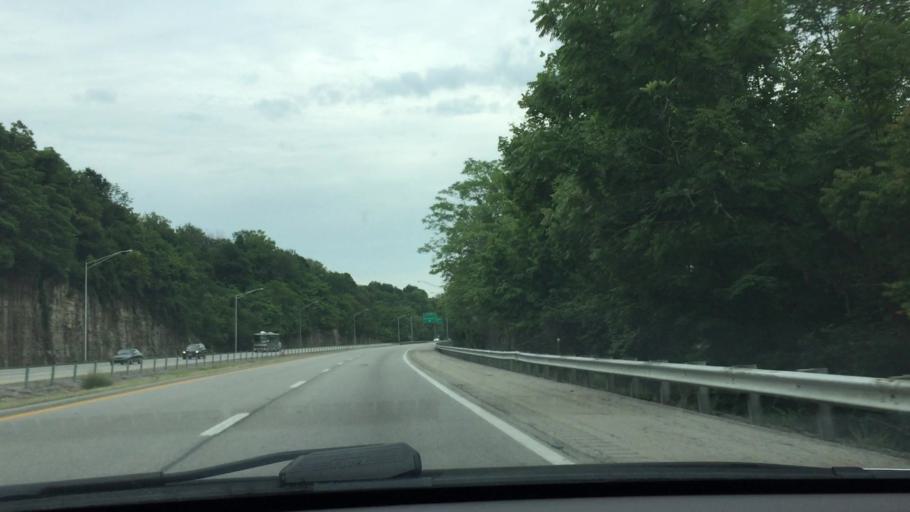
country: US
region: Kentucky
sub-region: Jefferson County
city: Indian Hills Cherokee Section
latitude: 38.2931
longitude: -85.6552
